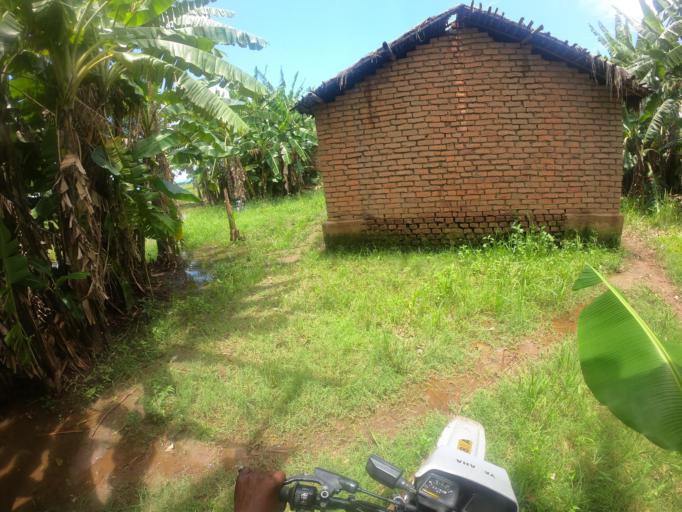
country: TZ
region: Mbeya
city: Kyela
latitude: -9.6650
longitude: 33.8244
